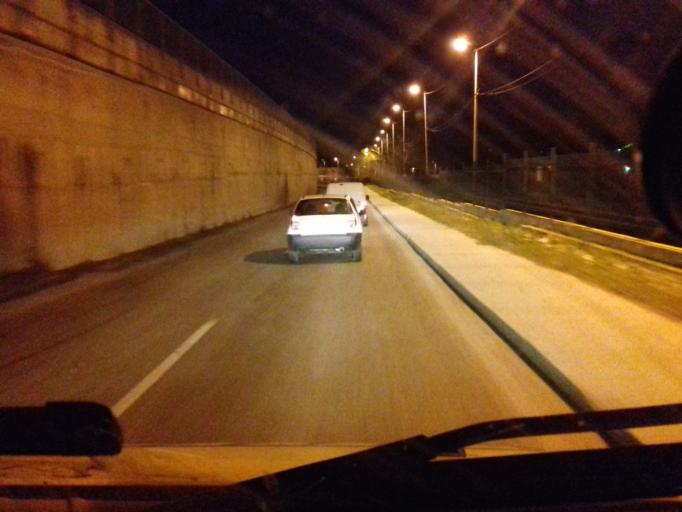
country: BA
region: Federation of Bosnia and Herzegovina
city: Dobrinje
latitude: 44.0903
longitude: 18.1120
